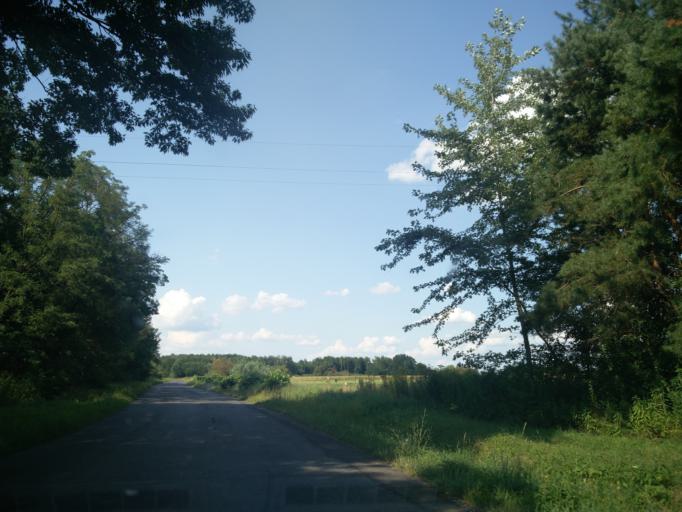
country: HU
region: Zala
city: Zalaegerszeg
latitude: 46.8681
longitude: 16.8031
